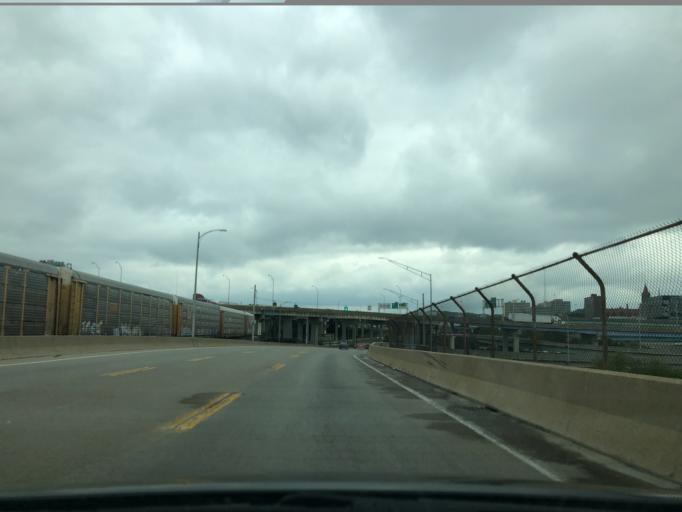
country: US
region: Kentucky
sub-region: Kenton County
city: Covington
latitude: 39.0945
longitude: -84.5204
